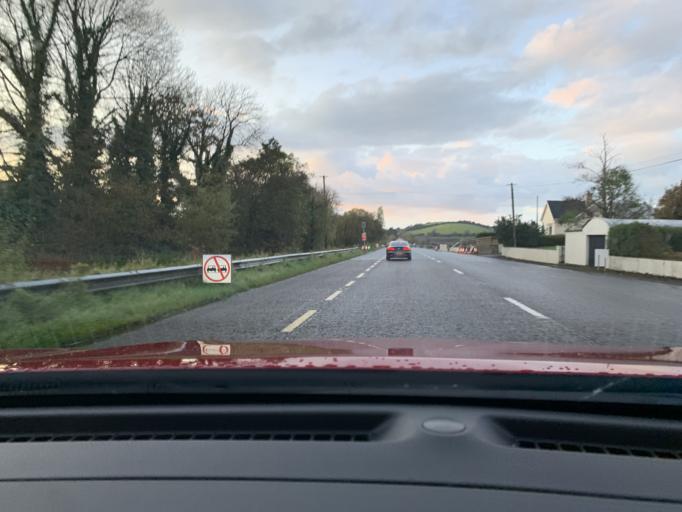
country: IE
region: Connaught
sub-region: Roscommon
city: Boyle
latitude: 54.0726
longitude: -8.3673
